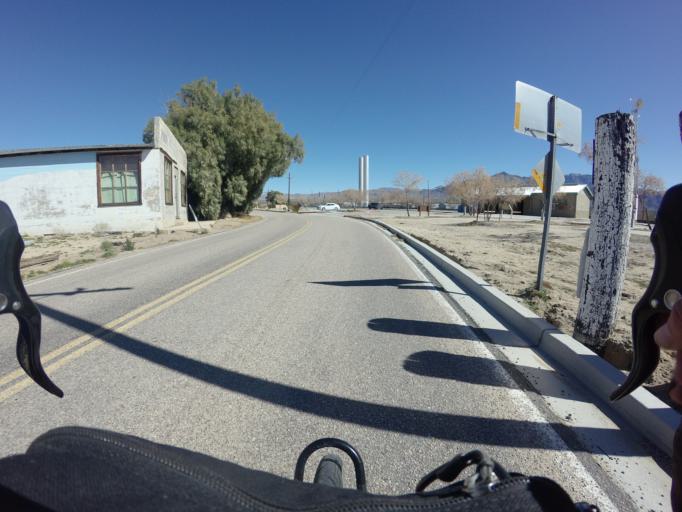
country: US
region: Nevada
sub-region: Clark County
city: Sandy Valley
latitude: 35.0125
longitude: -115.6528
